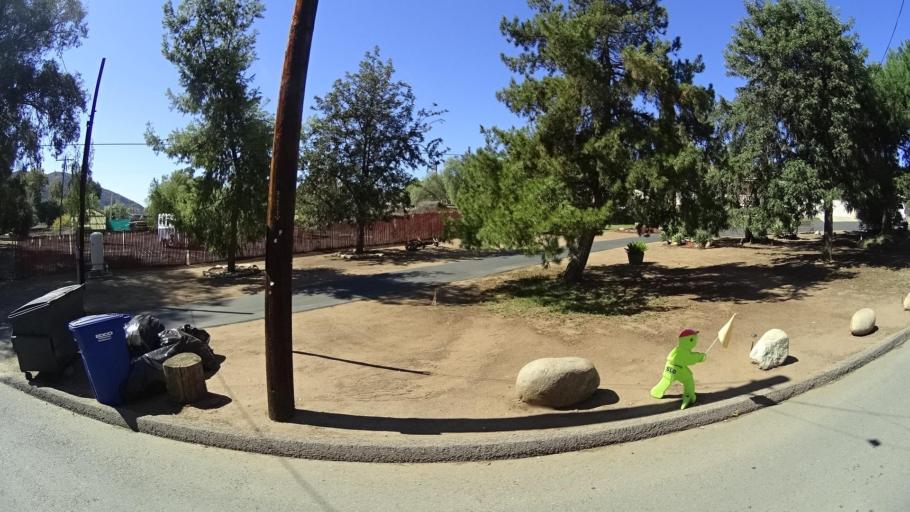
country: US
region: California
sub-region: San Diego County
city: Harbison Canyon
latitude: 32.8635
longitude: -116.8346
